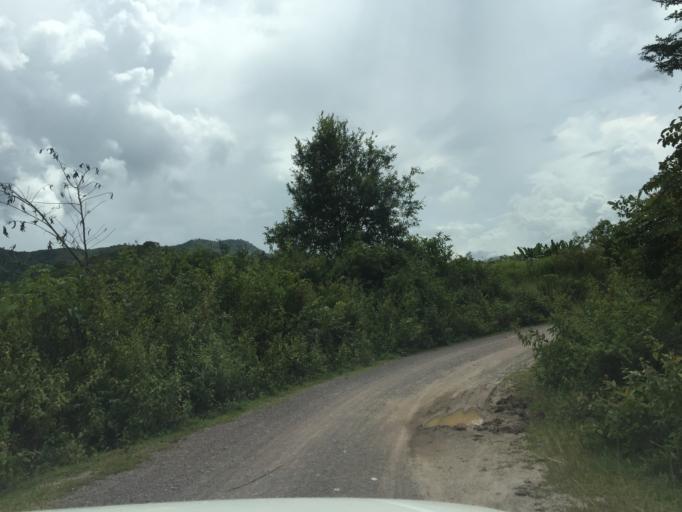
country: LA
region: Xiangkhoang
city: Muang Phonsavan
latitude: 19.3410
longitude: 103.5501
